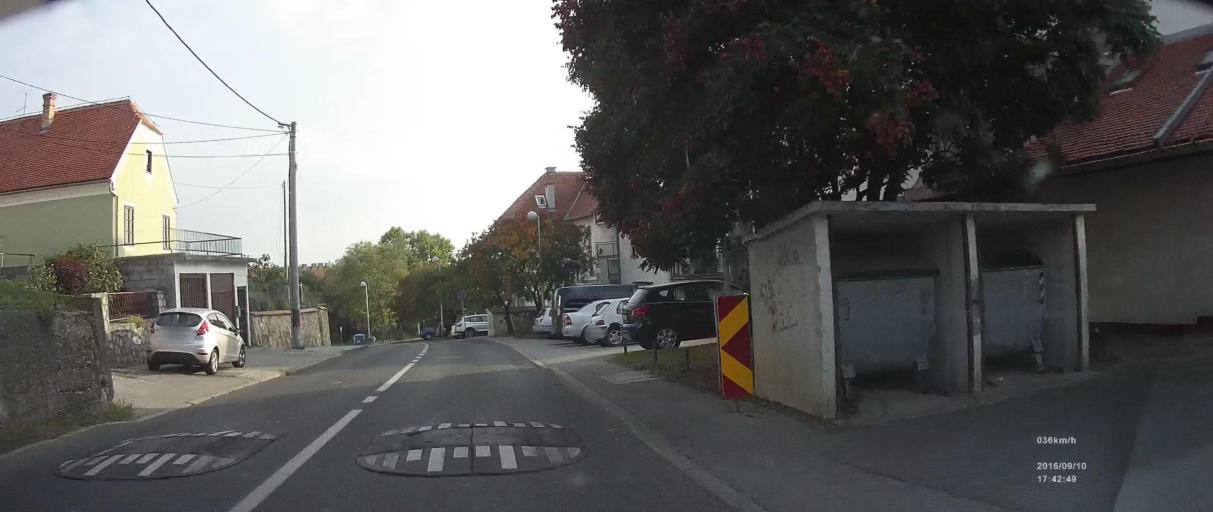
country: HR
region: Grad Zagreb
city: Zagreb - Centar
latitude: 45.8268
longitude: 15.9379
